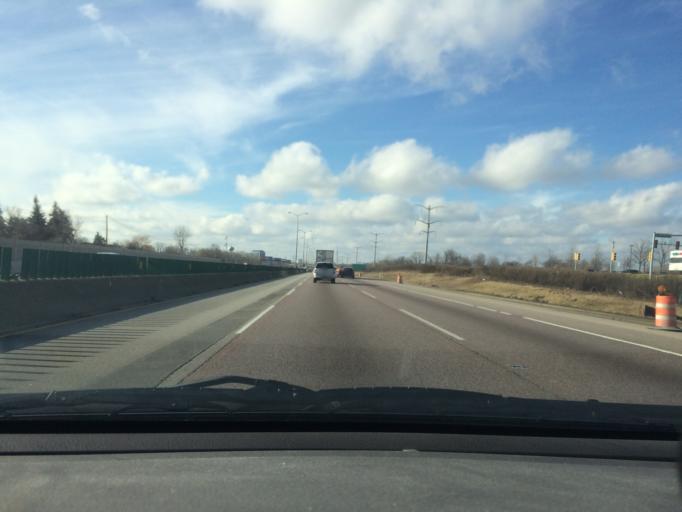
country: US
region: Illinois
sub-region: Cook County
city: South Barrington
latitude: 42.0666
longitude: -88.1205
